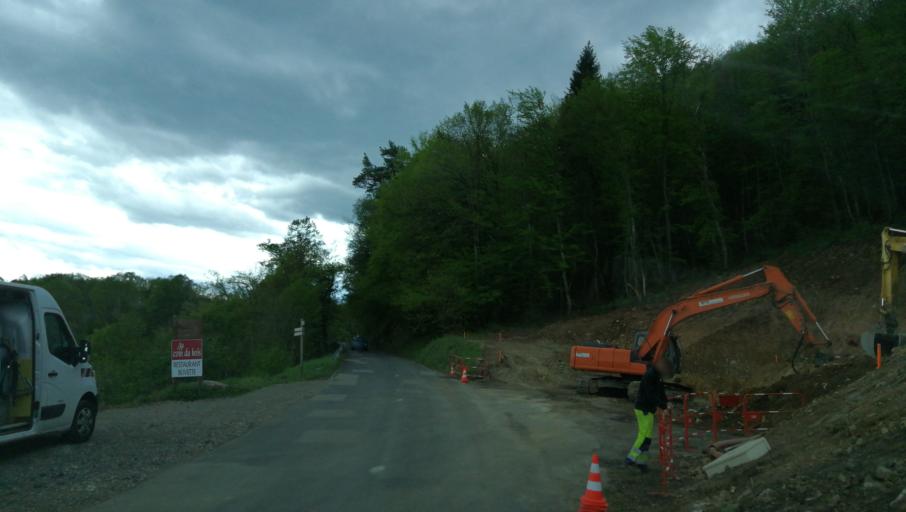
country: FR
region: Rhone-Alpes
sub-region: Departement de la Savoie
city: Brison-Saint-Innocent
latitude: 45.7000
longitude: 5.8553
